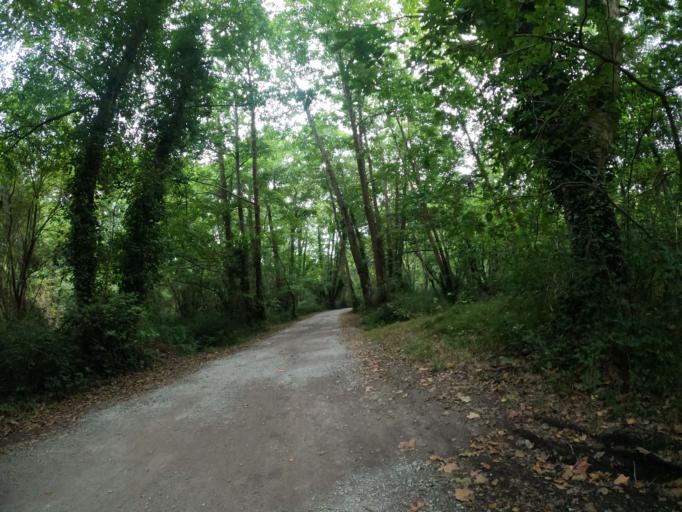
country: FR
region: Aquitaine
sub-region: Departement des Landes
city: Leon
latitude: 43.8864
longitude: -1.3080
